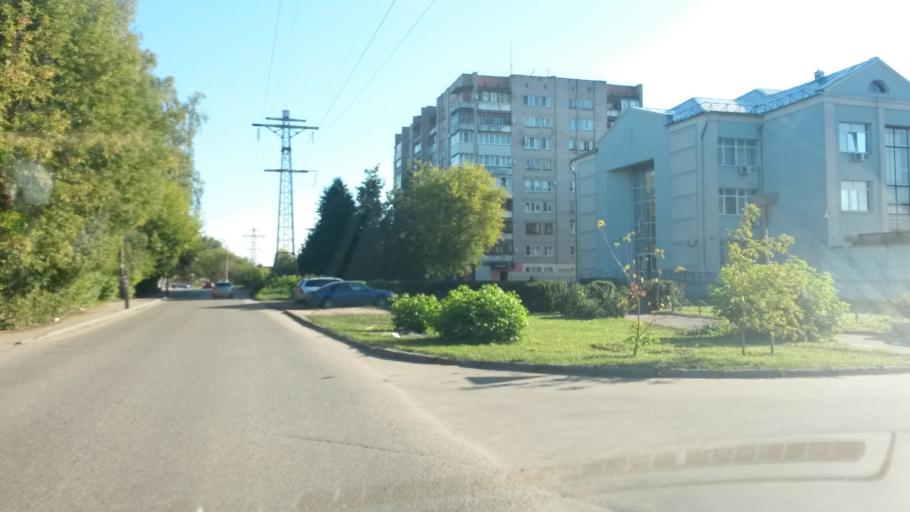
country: RU
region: Ivanovo
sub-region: Gorod Ivanovo
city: Ivanovo
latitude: 56.9989
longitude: 40.9593
